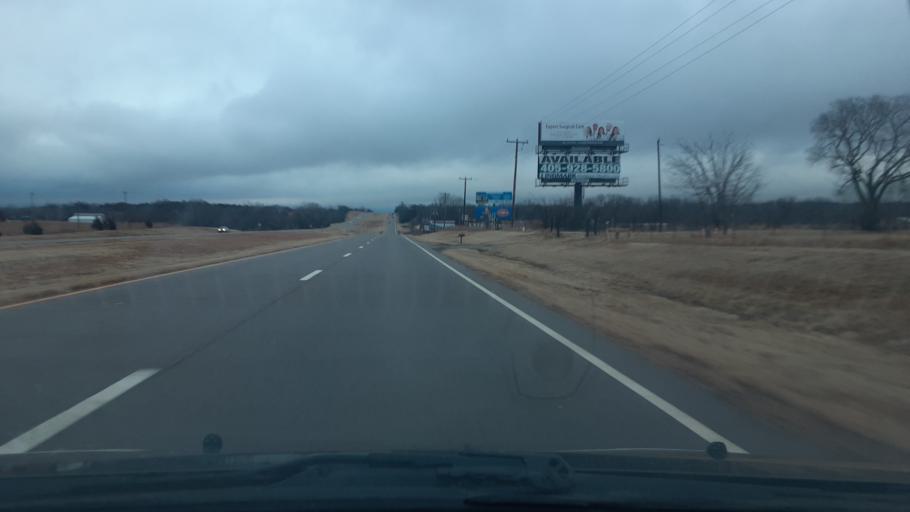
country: US
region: Oklahoma
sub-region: Payne County
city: Stillwater
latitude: 36.1158
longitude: -97.1614
